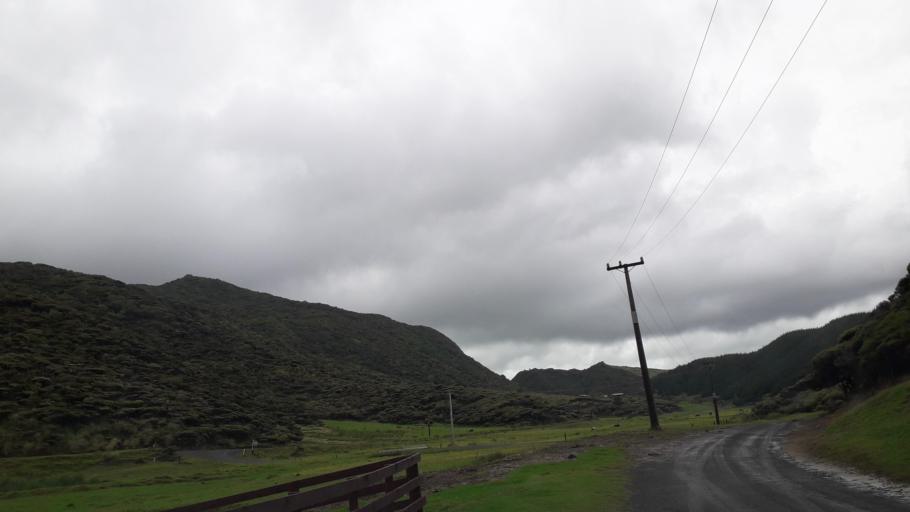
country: NZ
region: Northland
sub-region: Far North District
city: Ahipara
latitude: -35.4394
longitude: 173.2867
